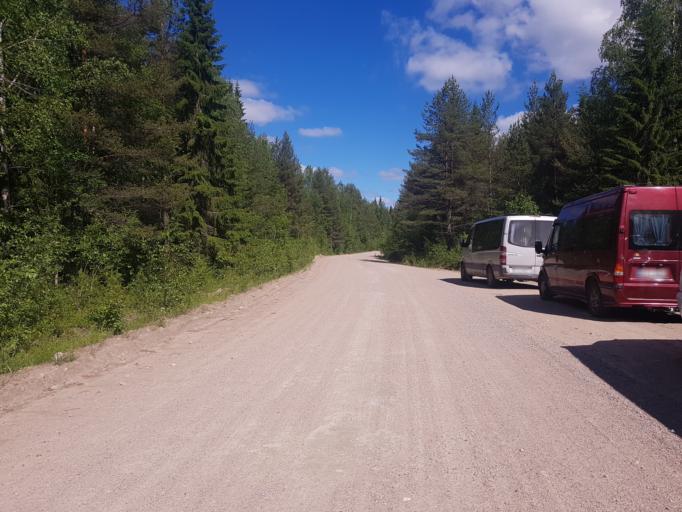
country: RU
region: Republic of Karelia
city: Kalevala
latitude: 65.2607
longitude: 30.9320
